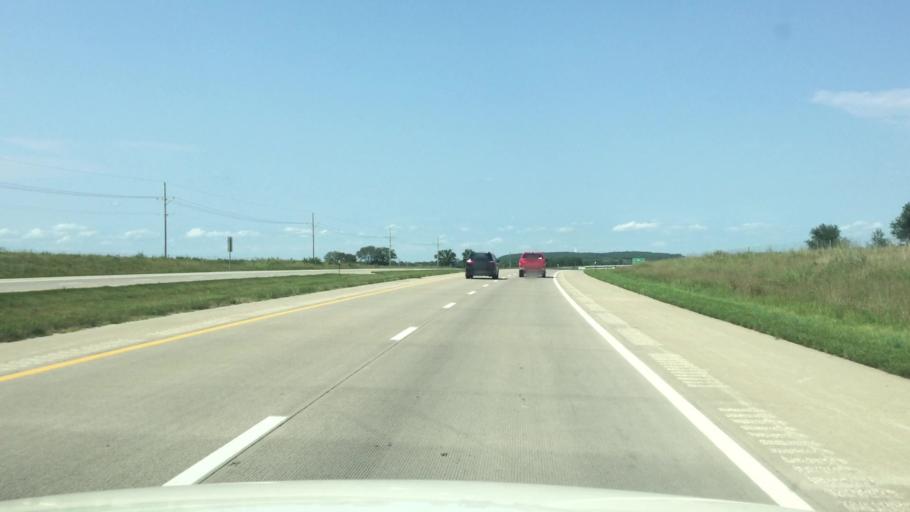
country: US
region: Kansas
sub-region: Linn County
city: Pleasanton
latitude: 38.2113
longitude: -94.7048
